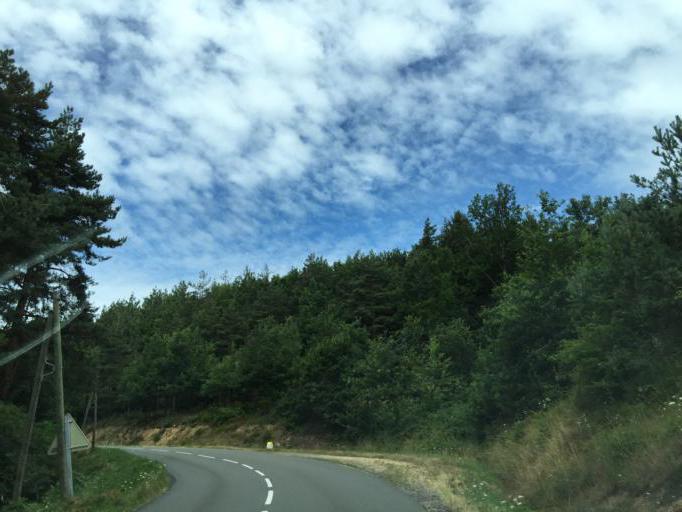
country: FR
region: Rhone-Alpes
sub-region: Departement de la Loire
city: Saint-Bonnet-le-Chateau
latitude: 45.4104
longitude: 4.0992
